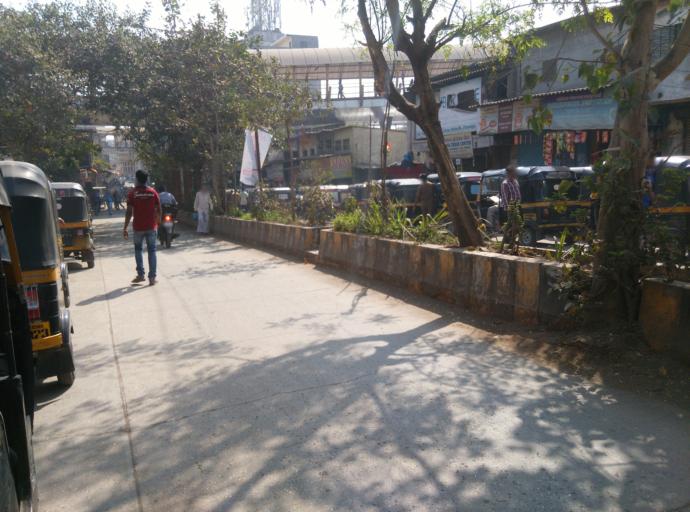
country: IN
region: Maharashtra
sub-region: Thane
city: Ulhasnagar
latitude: 19.2195
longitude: 73.1625
